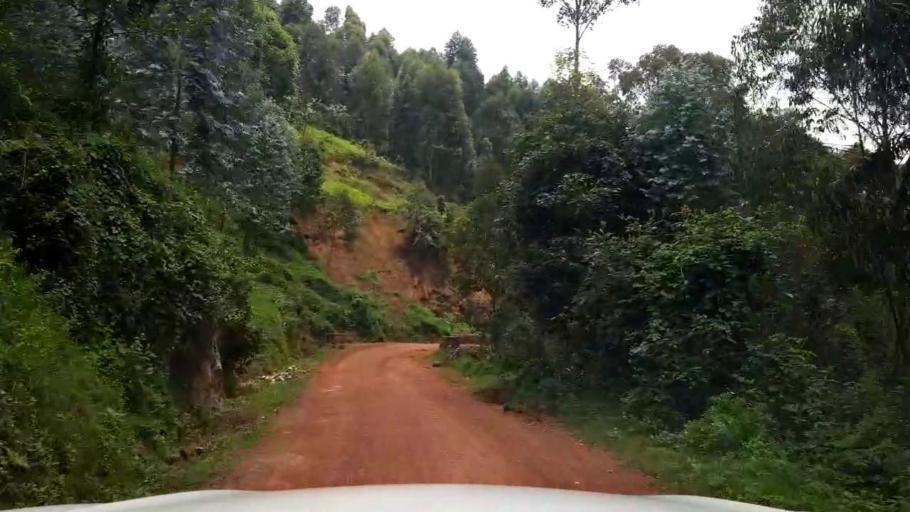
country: RW
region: Northern Province
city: Byumba
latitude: -1.4790
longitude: 29.9030
